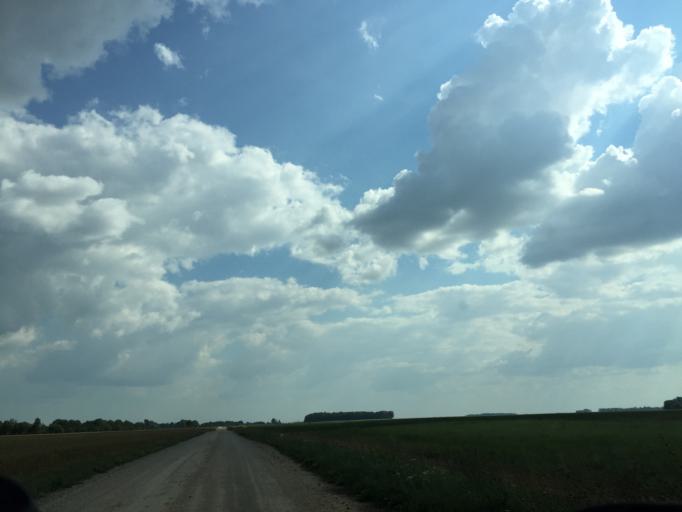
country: LV
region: Jelgava
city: Jelgava
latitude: 56.5017
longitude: 23.7572
